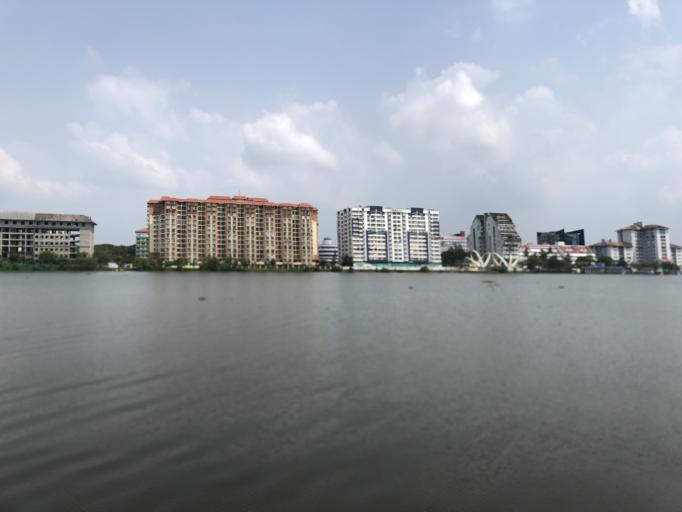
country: IN
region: Kerala
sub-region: Ernakulam
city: Cochin
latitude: 9.9867
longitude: 76.2680
